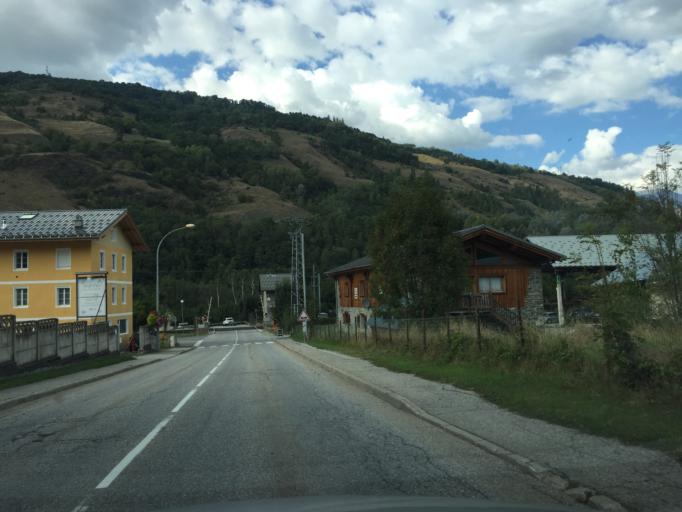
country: FR
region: Rhone-Alpes
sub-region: Departement de la Savoie
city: Bourg-Saint-Maurice
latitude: 45.5745
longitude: 6.7363
